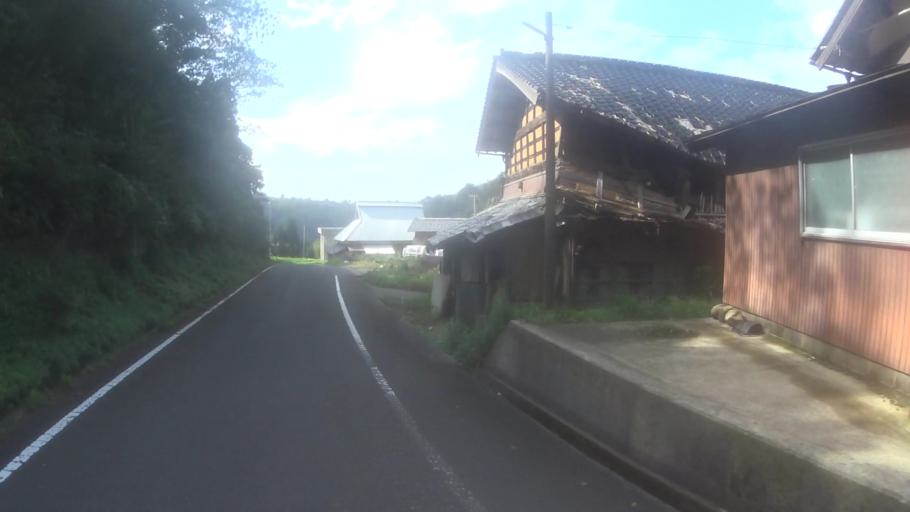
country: JP
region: Kyoto
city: Miyazu
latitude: 35.6051
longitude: 135.1609
